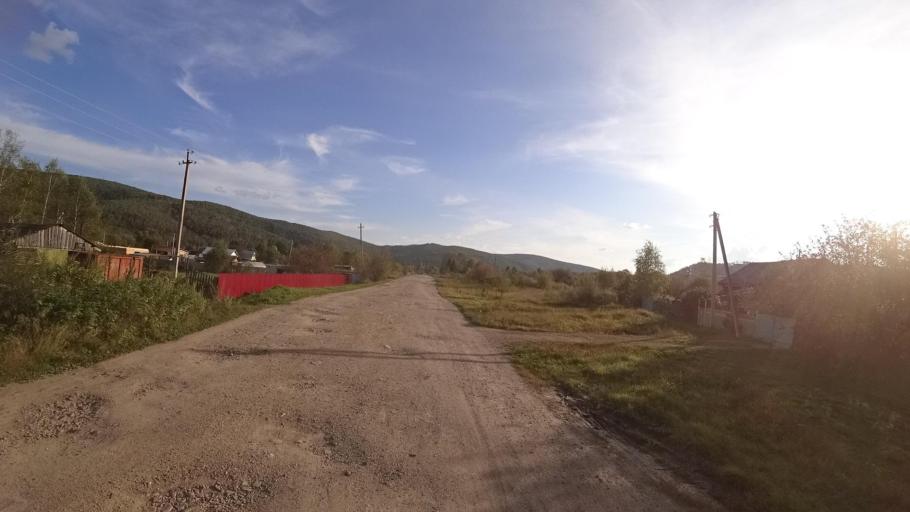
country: RU
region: Jewish Autonomous Oblast
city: Kul'dur
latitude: 49.2008
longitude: 131.6265
